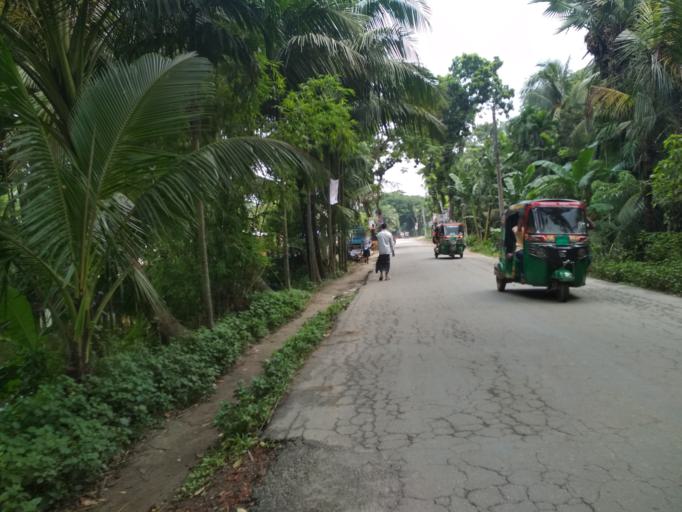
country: BD
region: Chittagong
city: Lakshmipur
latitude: 22.9479
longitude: 90.8085
